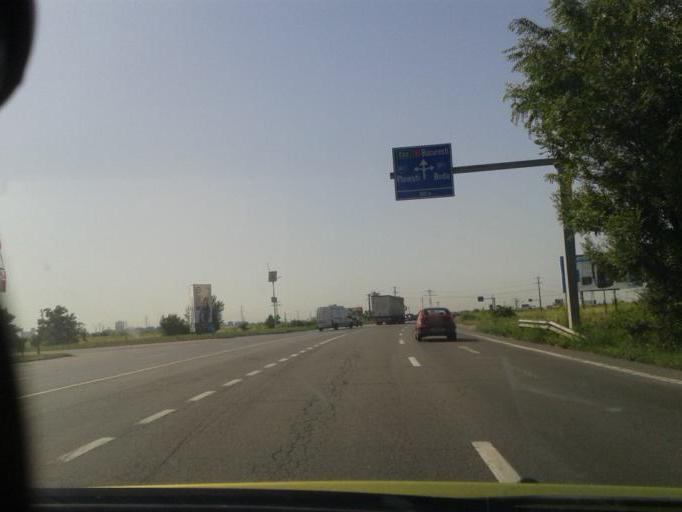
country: RO
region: Prahova
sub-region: Comuna Paulesti
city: Paulesti
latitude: 44.9648
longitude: 25.9643
